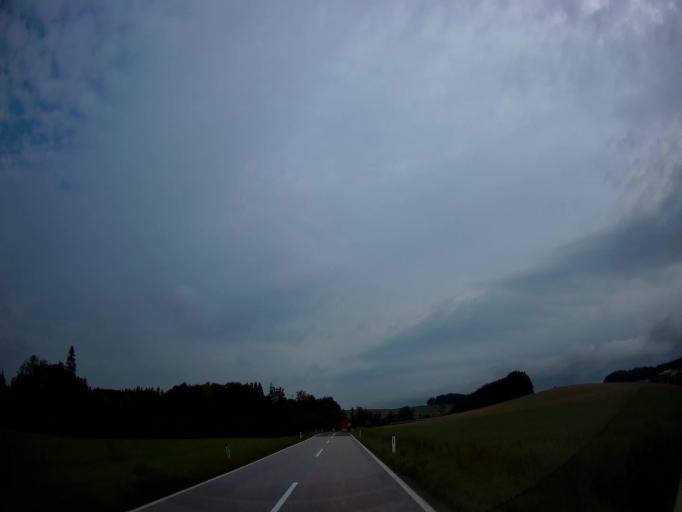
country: AT
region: Salzburg
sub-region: Politischer Bezirk Salzburg-Umgebung
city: Mattsee
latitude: 48.0225
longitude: 13.1328
